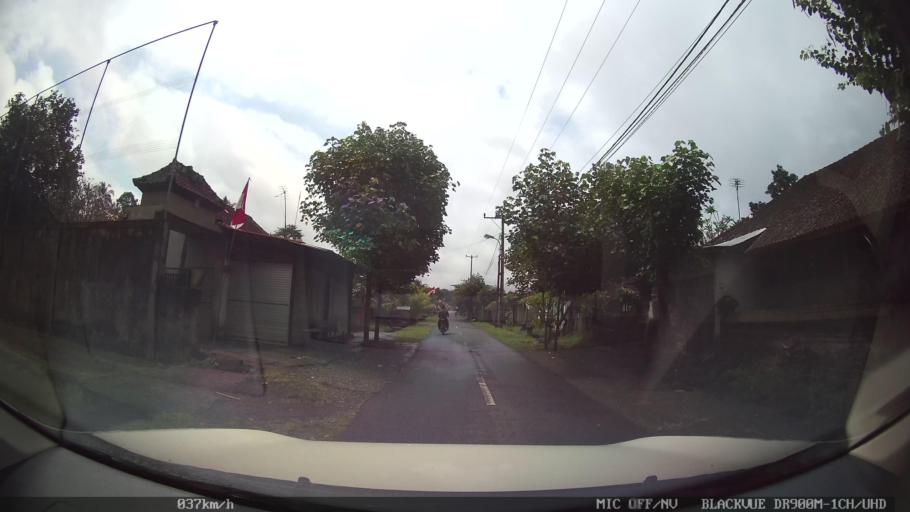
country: ID
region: Bali
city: Pegongan
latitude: -8.4868
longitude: 115.2266
